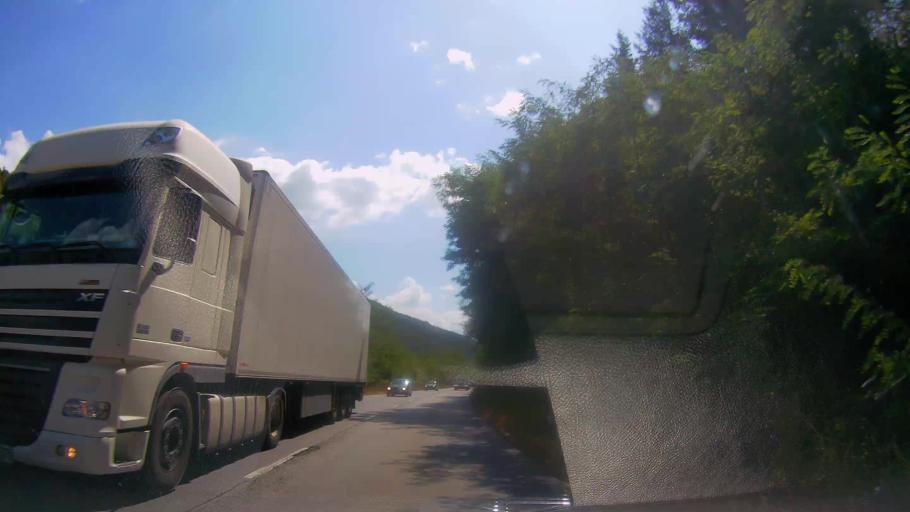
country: BG
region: Stara Zagora
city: Gurkovo
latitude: 42.7574
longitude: 25.7079
